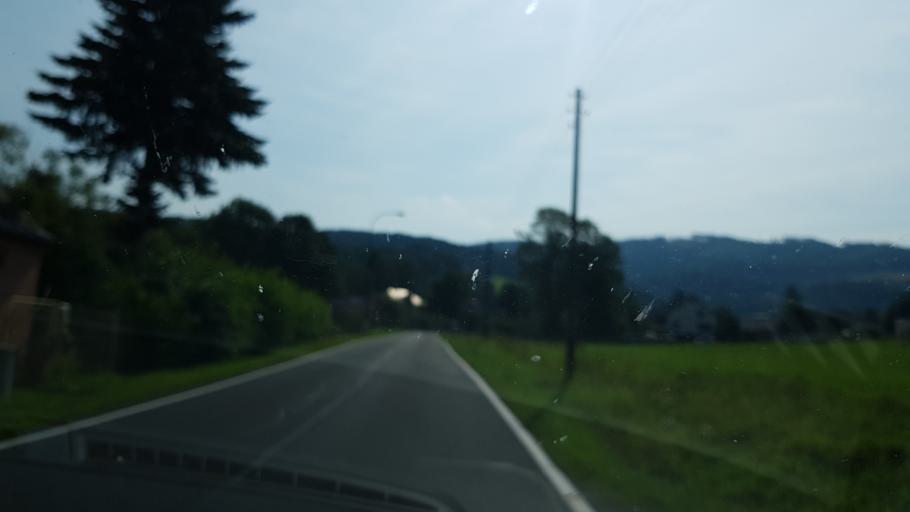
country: CZ
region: Olomoucky
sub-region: Okres Jesenik
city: Jesenik
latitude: 50.2139
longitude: 17.2228
